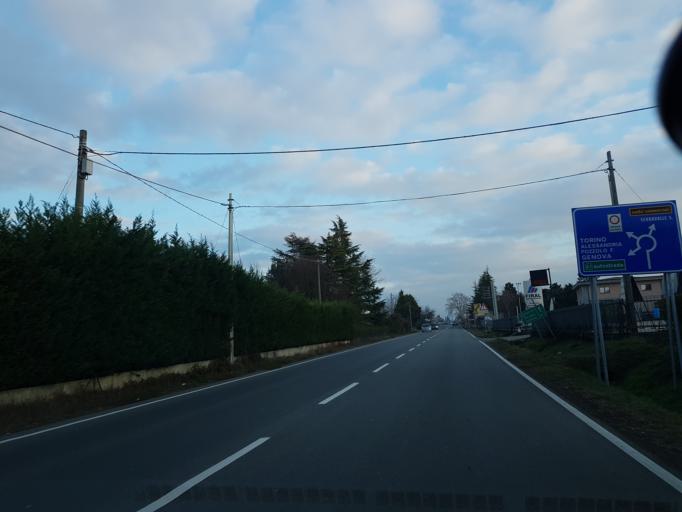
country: IT
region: Piedmont
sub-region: Provincia di Alessandria
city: Novi Ligure
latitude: 44.7518
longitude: 8.8051
